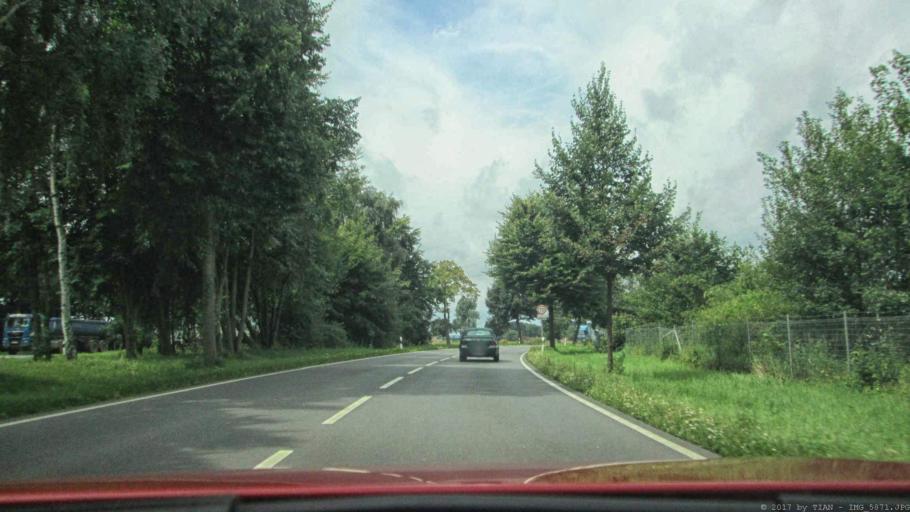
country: DE
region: Lower Saxony
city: Bad Bevensen
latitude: 53.0709
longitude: 10.5677
